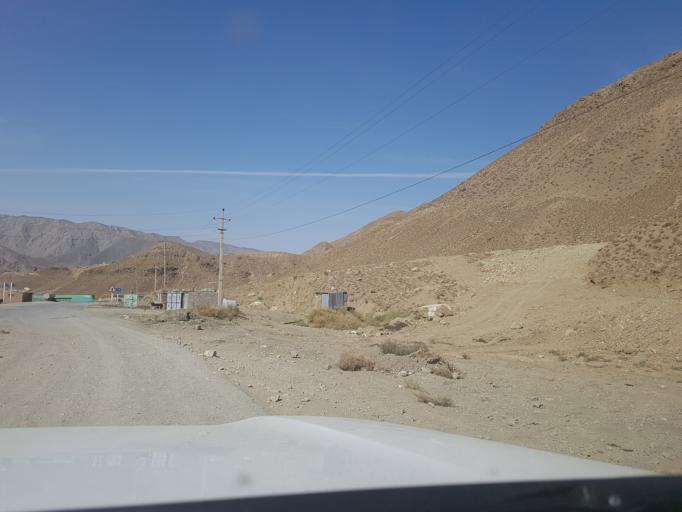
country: TM
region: Ahal
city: Baharly
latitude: 38.4542
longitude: 57.0448
